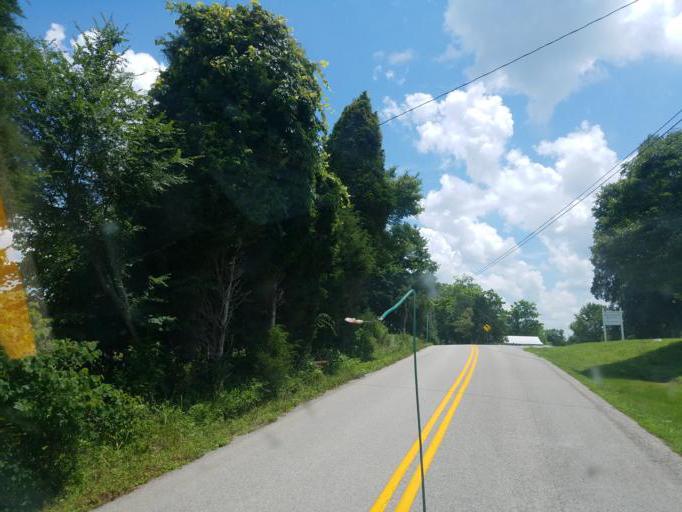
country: US
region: Kentucky
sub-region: Grayson County
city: Leitchfield
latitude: 37.4832
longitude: -86.4159
